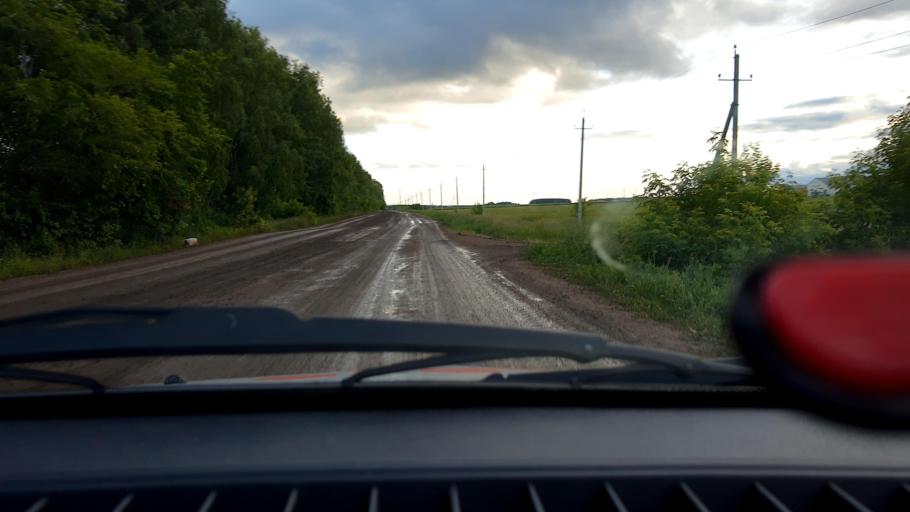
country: RU
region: Bashkortostan
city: Tolbazy
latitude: 54.1935
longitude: 55.8818
